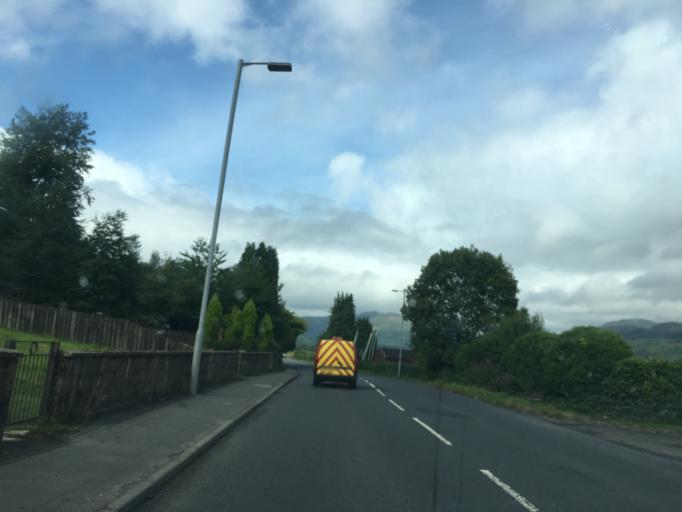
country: GB
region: Scotland
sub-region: Argyll and Bute
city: Dunoon
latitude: 55.9851
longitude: -4.9539
